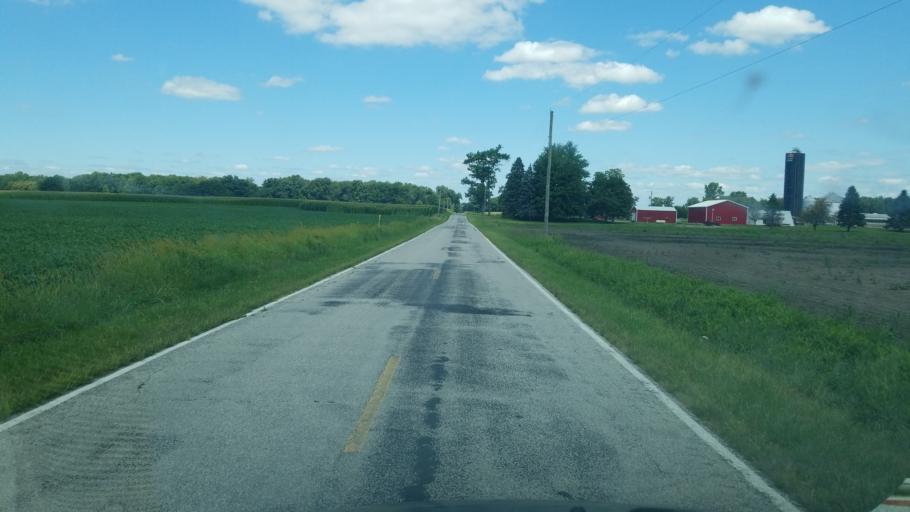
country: US
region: Ohio
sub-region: Fulton County
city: Delta
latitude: 41.6211
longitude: -84.0151
